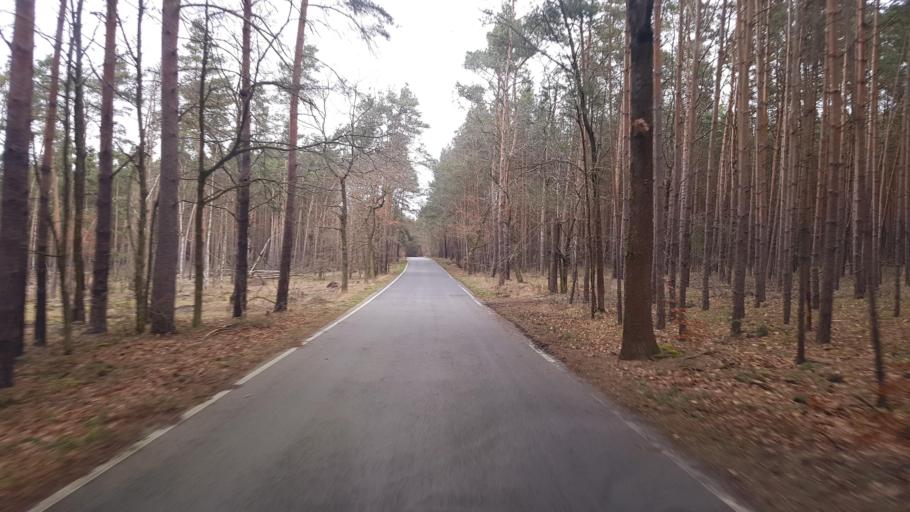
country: DE
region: Brandenburg
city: Kroppen
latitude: 51.3712
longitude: 13.7915
